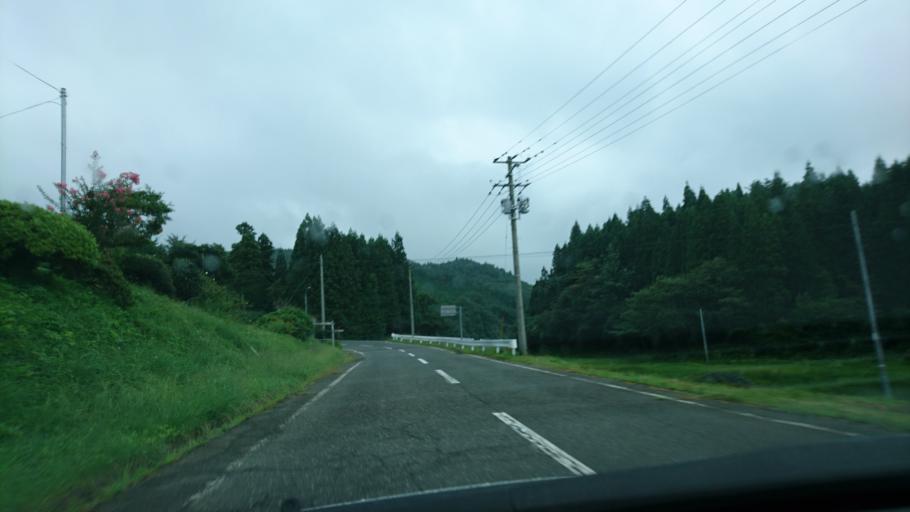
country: JP
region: Iwate
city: Ichinoseki
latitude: 38.8835
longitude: 140.9736
